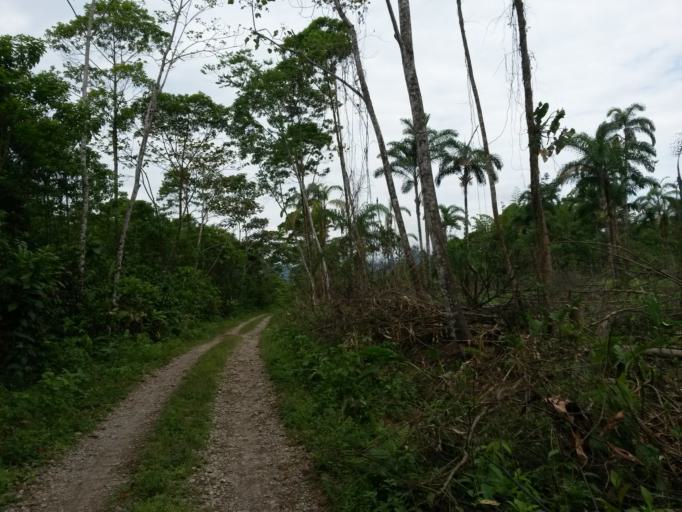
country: CO
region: Putumayo
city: Puerto Guzman
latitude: 1.0194
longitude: -76.3729
